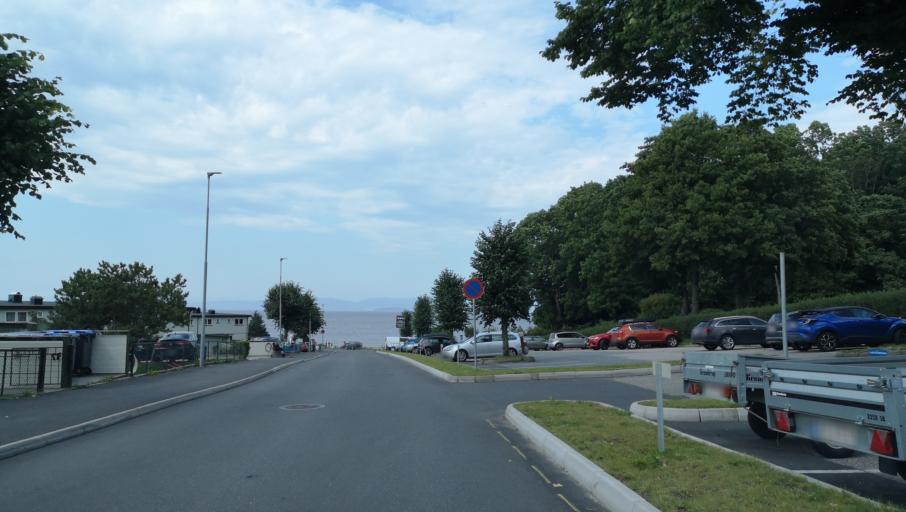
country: NO
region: Ostfold
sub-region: Moss
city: Moss
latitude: 59.4471
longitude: 10.6169
